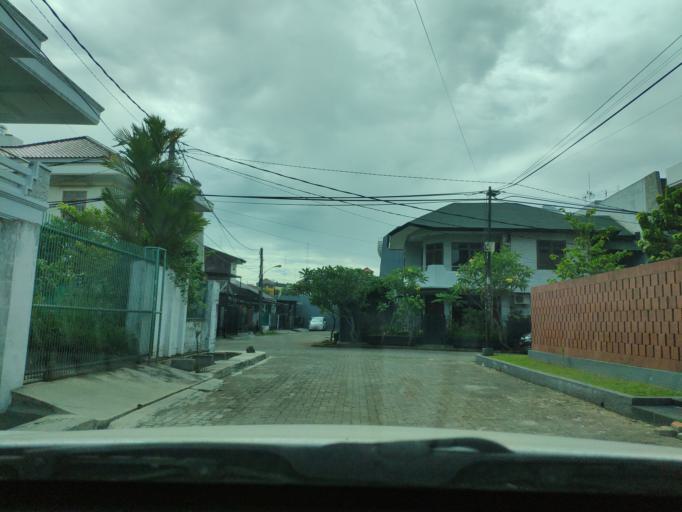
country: ID
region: West Java
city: Ciputat
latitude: -6.2222
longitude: 106.7117
